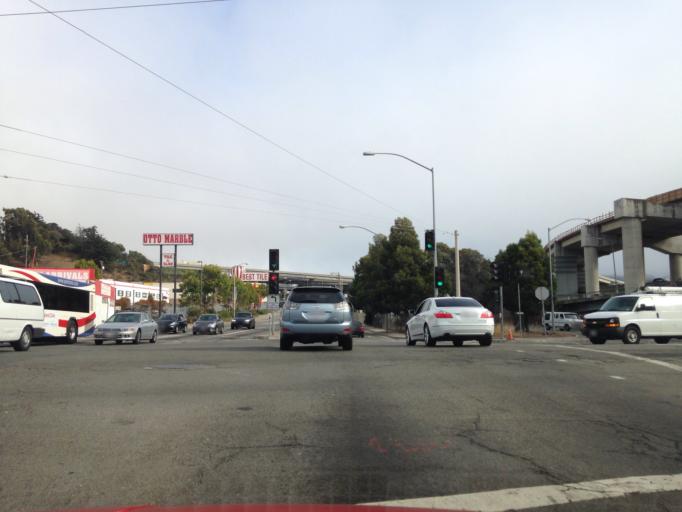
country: US
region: California
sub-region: San Francisco County
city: San Francisco
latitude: 37.7381
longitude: -122.4071
